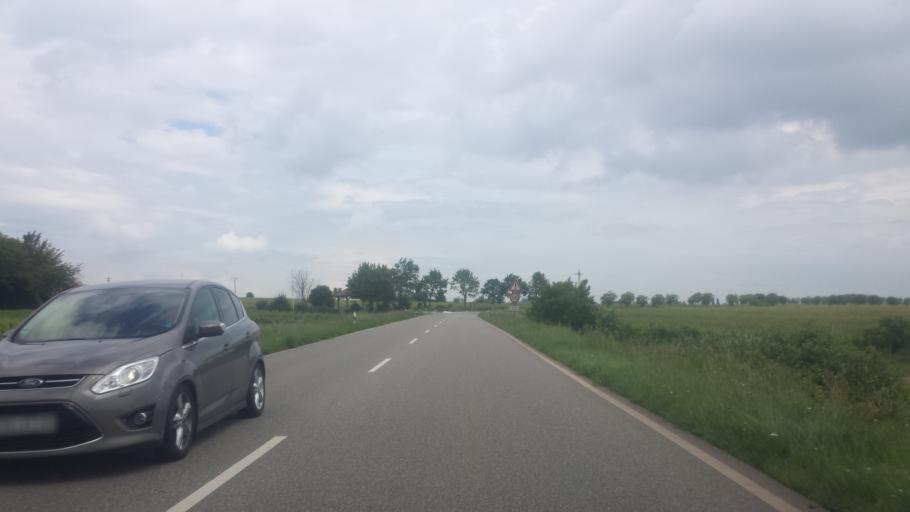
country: DE
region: Rheinland-Pfalz
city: Eschbach
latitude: 49.1729
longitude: 8.0225
